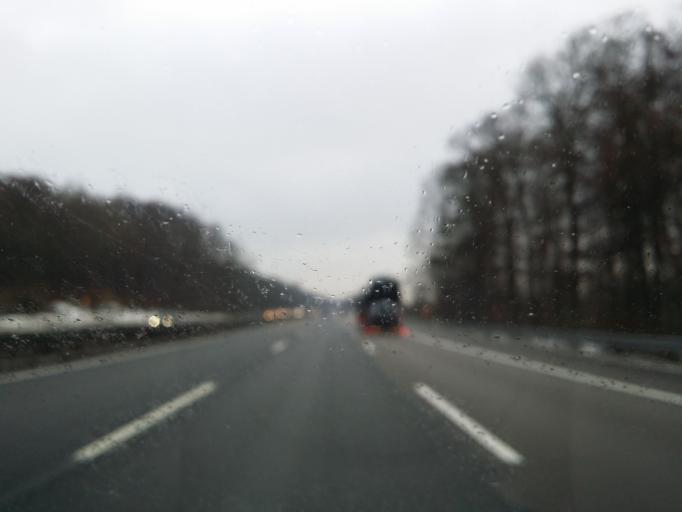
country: DE
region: Hesse
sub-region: Regierungsbezirk Darmstadt
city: Niedernhausen
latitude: 50.1353
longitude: 8.3342
